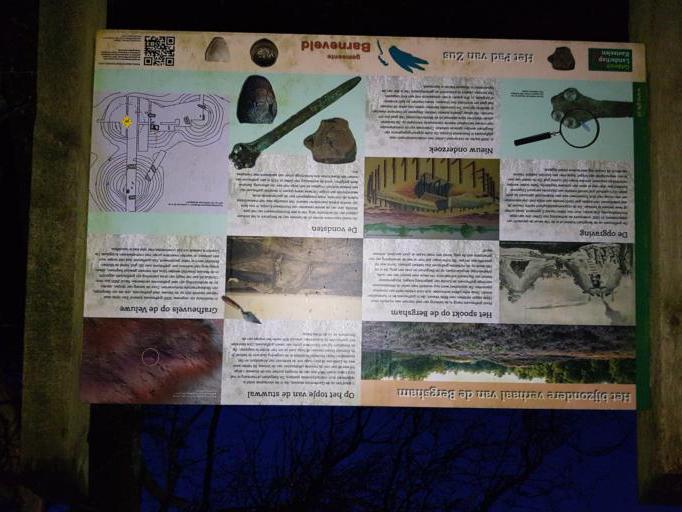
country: NL
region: Gelderland
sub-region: Gemeente Barneveld
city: Garderen
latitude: 52.2250
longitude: 5.6894
